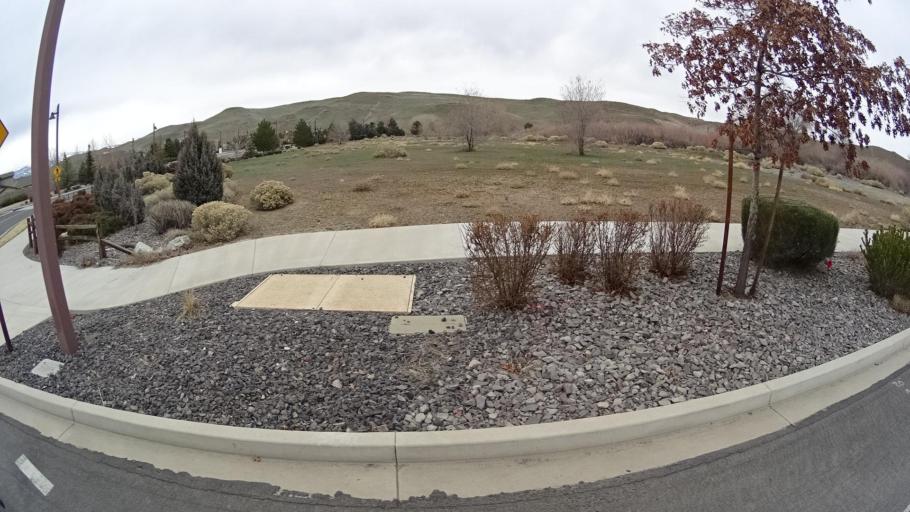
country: US
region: Nevada
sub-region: Washoe County
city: Spanish Springs
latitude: 39.6048
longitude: -119.7274
